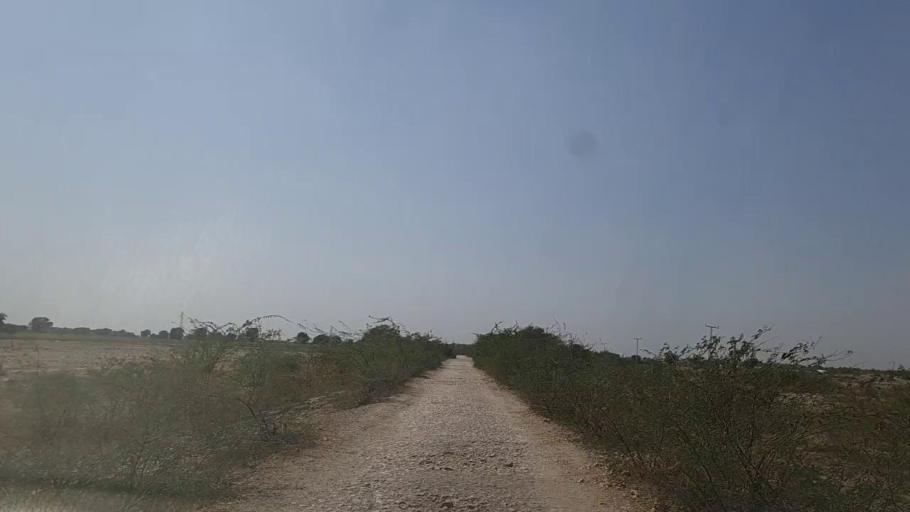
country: PK
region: Sindh
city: Naukot
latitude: 24.6516
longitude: 69.2828
